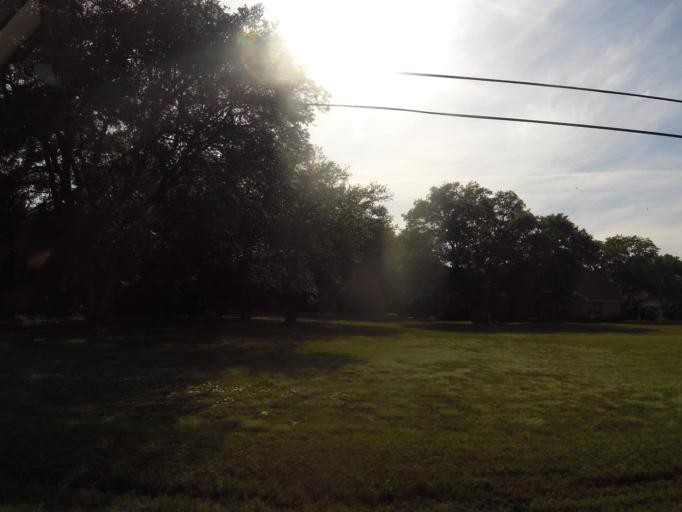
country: US
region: Florida
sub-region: Duval County
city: Atlantic Beach
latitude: 30.4677
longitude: -81.4864
